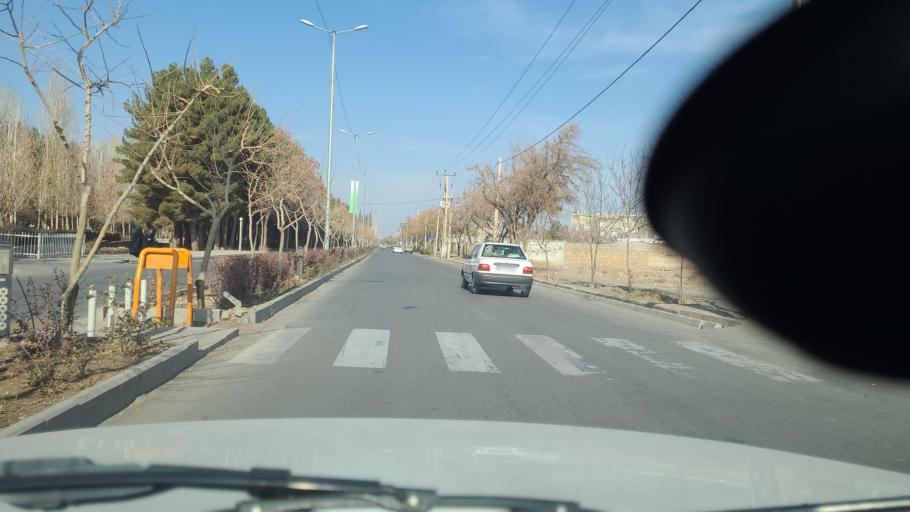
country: IR
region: Razavi Khorasan
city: Fariman
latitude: 35.6904
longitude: 59.8440
